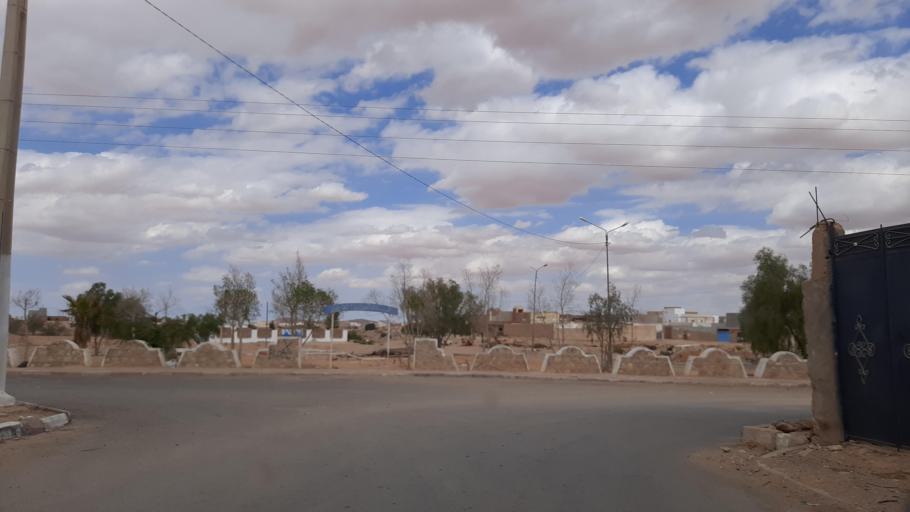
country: TN
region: Tataouine
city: Tataouine
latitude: 32.9433
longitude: 10.4578
